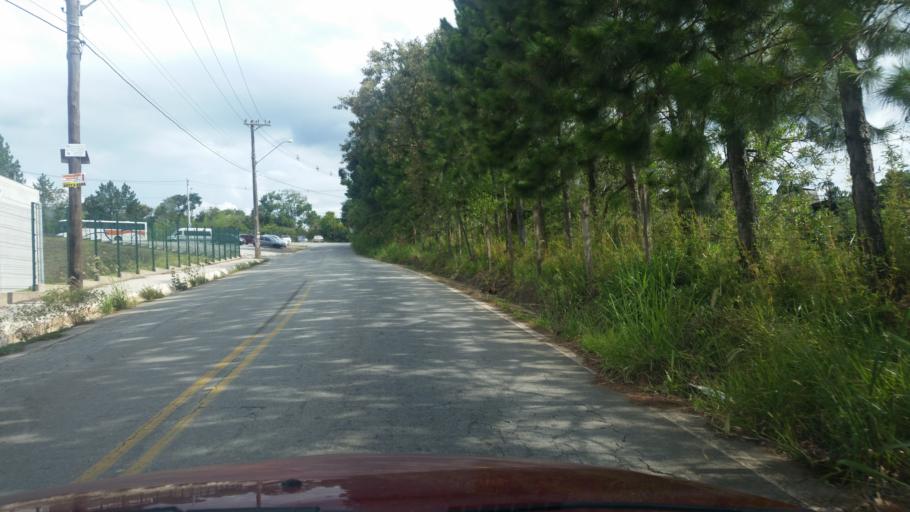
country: BR
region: Sao Paulo
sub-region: Sao Roque
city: Sao Roque
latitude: -23.4298
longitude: -47.1442
